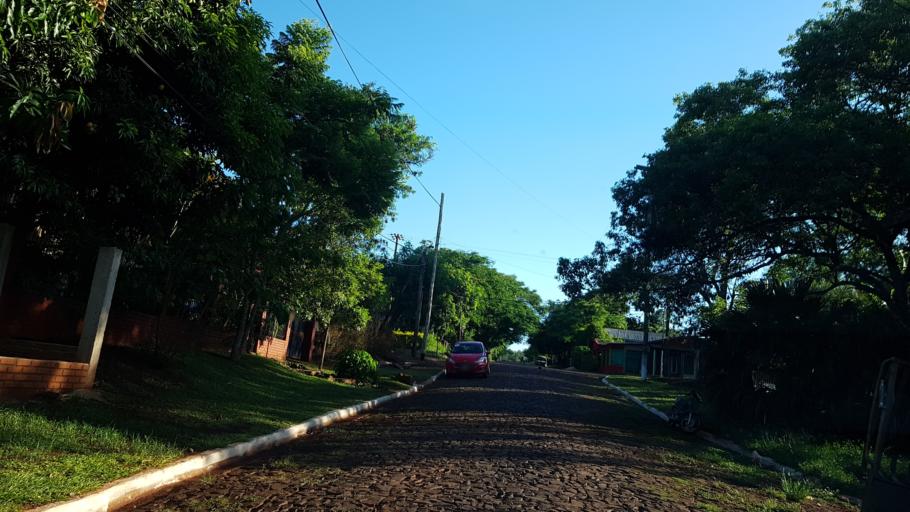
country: AR
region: Misiones
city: Puerto Libertad
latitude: -25.9203
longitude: -54.5870
